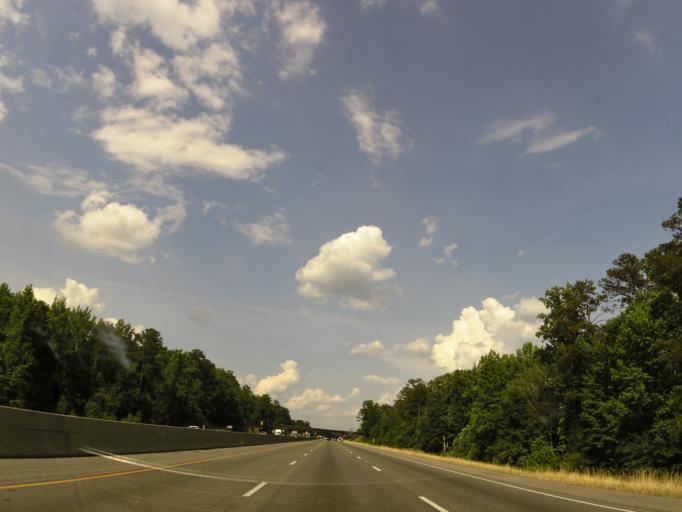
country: US
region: Alabama
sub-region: Tuscaloosa County
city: Coaling
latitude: 33.1795
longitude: -87.3735
